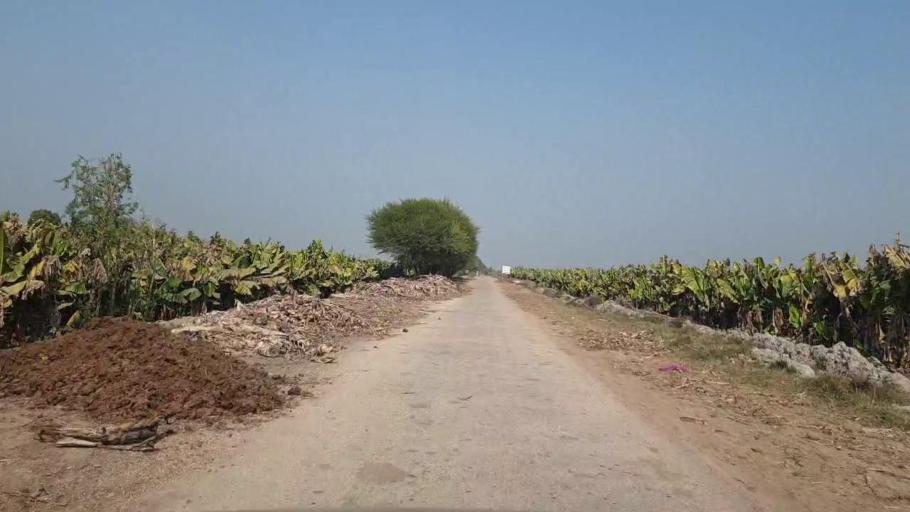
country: PK
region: Sindh
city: Bhit Shah
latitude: 25.7803
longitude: 68.4936
